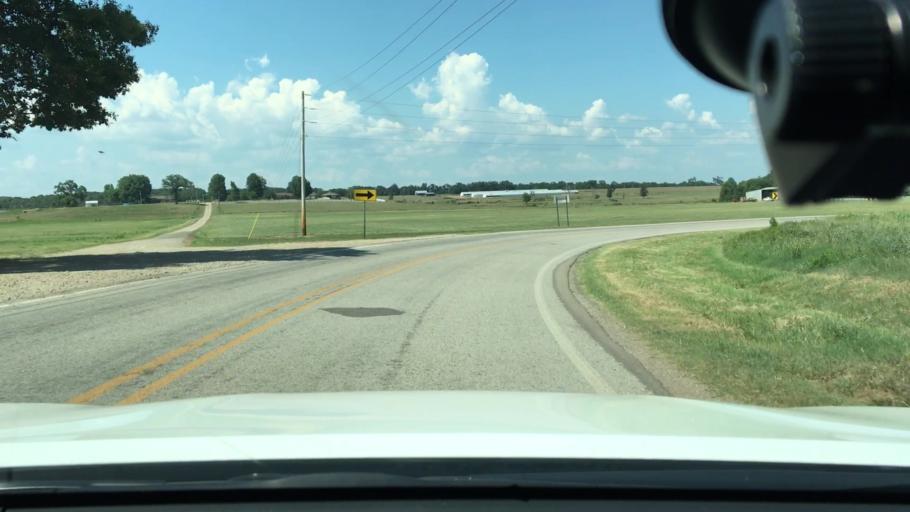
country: US
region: Arkansas
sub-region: Johnson County
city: Coal Hill
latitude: 35.3505
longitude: -93.5885
